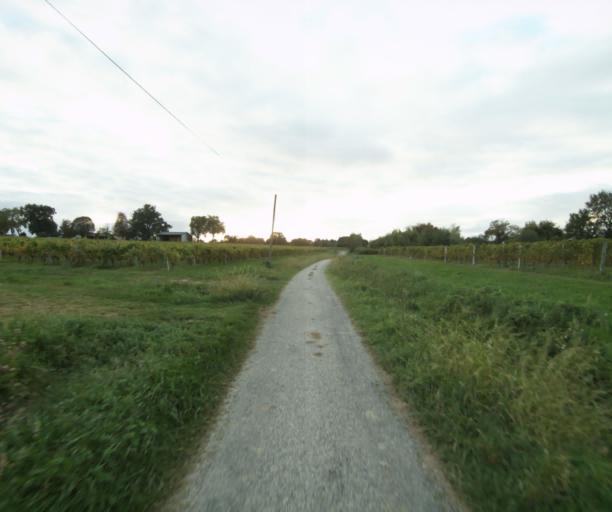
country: FR
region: Aquitaine
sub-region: Departement des Landes
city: Gabarret
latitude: 43.9718
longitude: 0.0963
